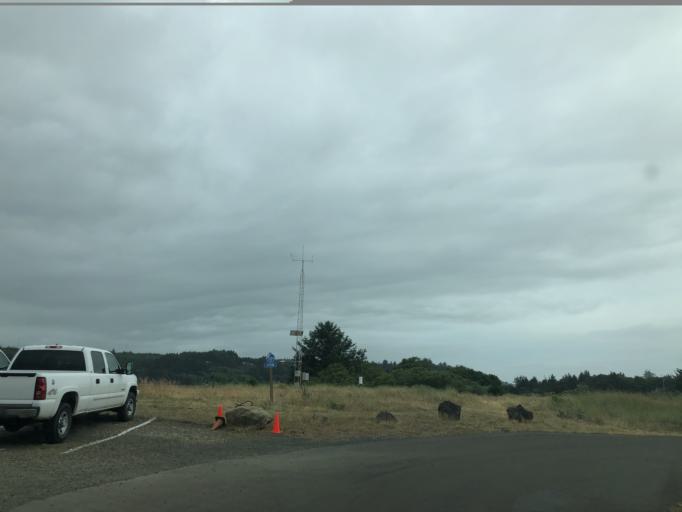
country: US
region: Oregon
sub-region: Lincoln County
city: Newport
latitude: 44.6210
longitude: -124.0435
